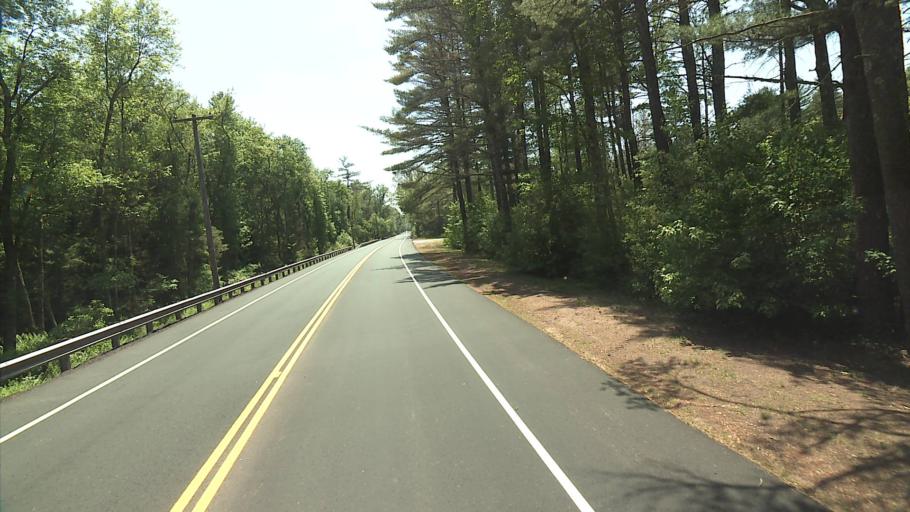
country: US
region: Connecticut
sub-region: Tolland County
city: Crystal Lake
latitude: 41.9599
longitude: -72.3659
